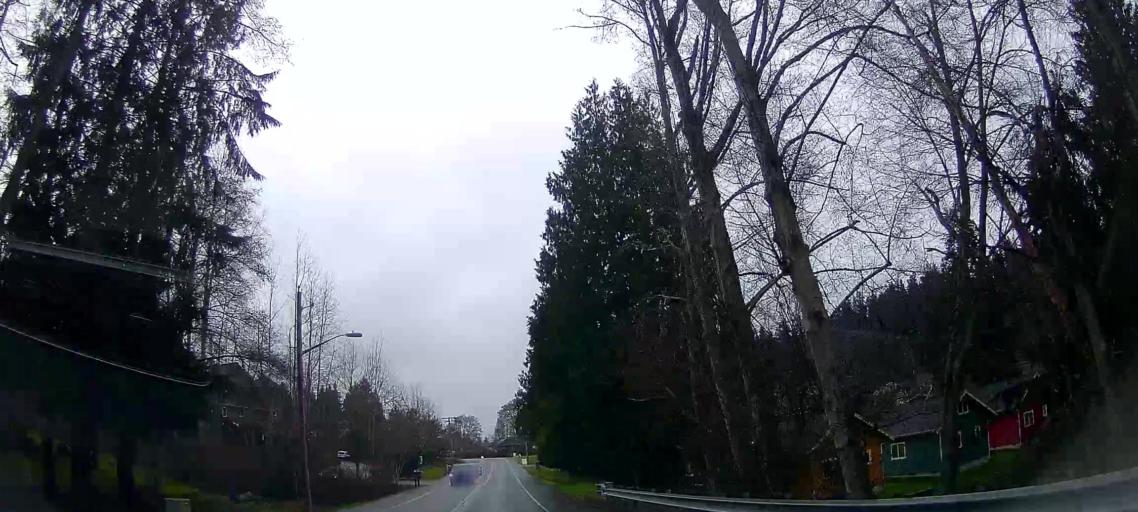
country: US
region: Washington
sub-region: Island County
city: Freeland
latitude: 48.0099
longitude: -122.5162
